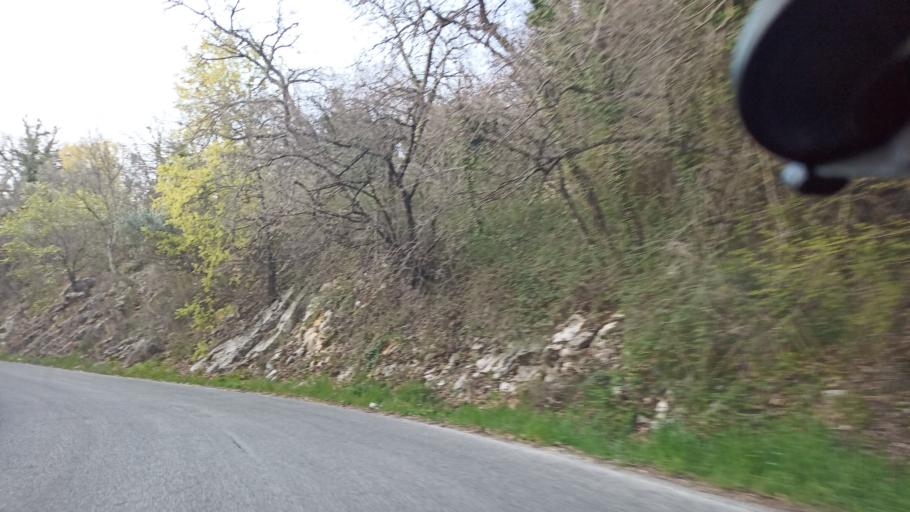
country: IT
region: Latium
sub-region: Provincia di Rieti
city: Cottanello
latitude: 42.4078
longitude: 12.6828
